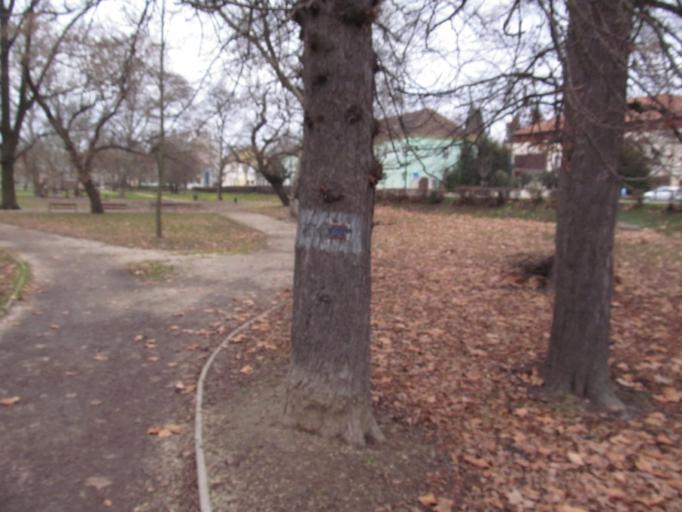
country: HU
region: Vas
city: Sarvar
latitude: 47.2516
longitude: 16.9388
